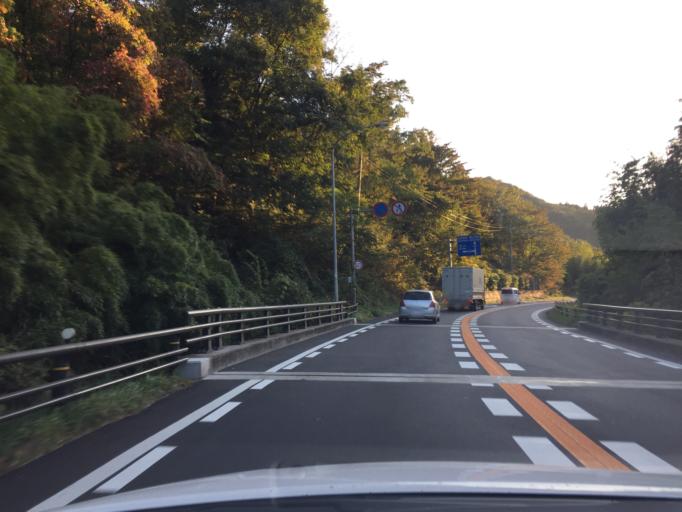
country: JP
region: Fukushima
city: Sukagawa
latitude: 37.2999
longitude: 140.4976
